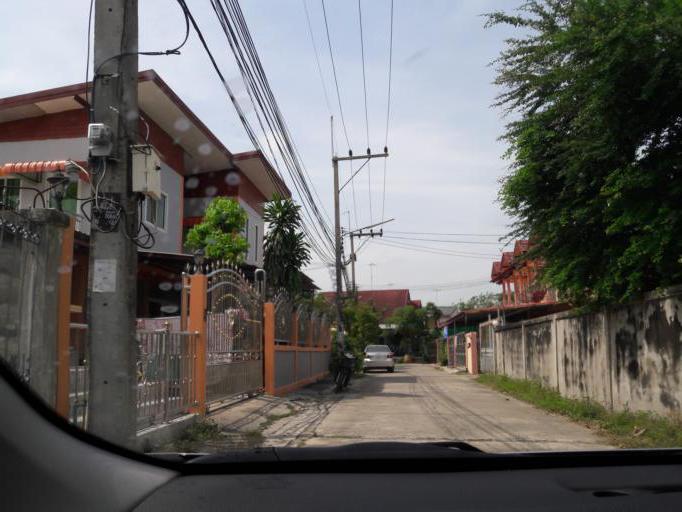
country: TH
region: Ang Thong
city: Ang Thong
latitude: 14.5741
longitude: 100.4560
